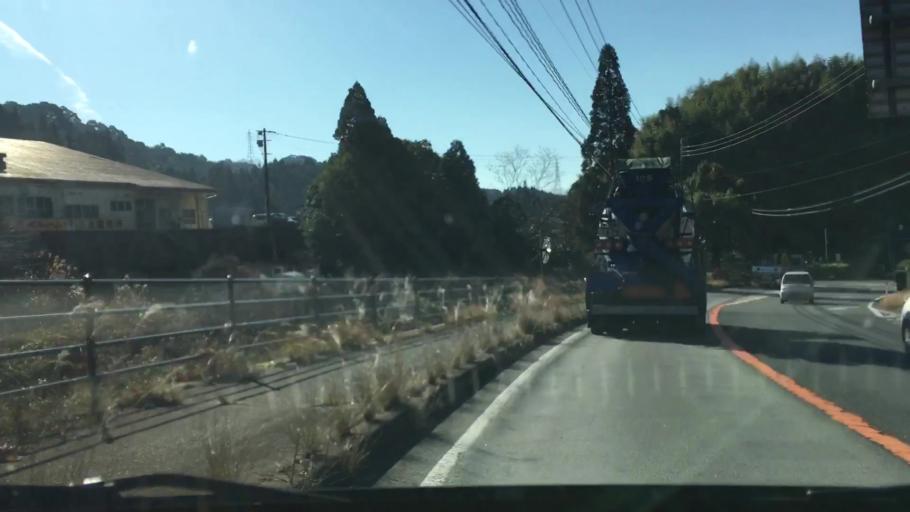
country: JP
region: Kagoshima
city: Kajiki
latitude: 31.7543
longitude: 130.6784
